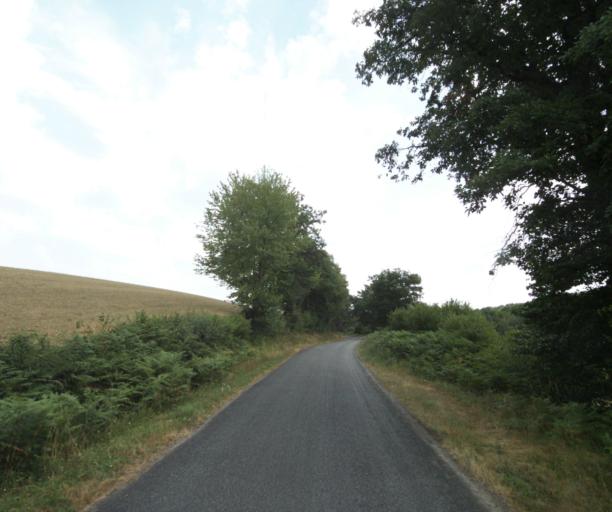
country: FR
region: Bourgogne
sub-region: Departement de Saone-et-Loire
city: Gueugnon
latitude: 46.5874
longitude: 4.0175
